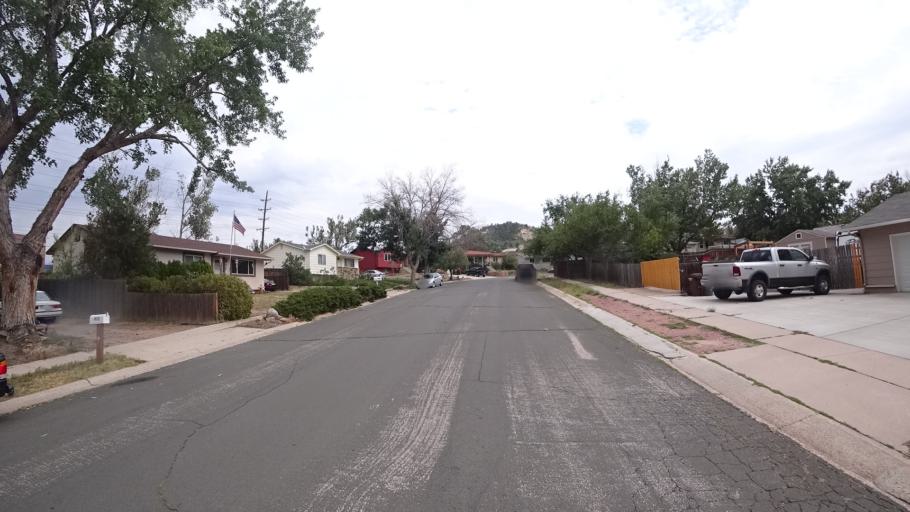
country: US
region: Colorado
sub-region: El Paso County
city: Colorado Springs
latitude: 38.8964
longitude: -104.8103
